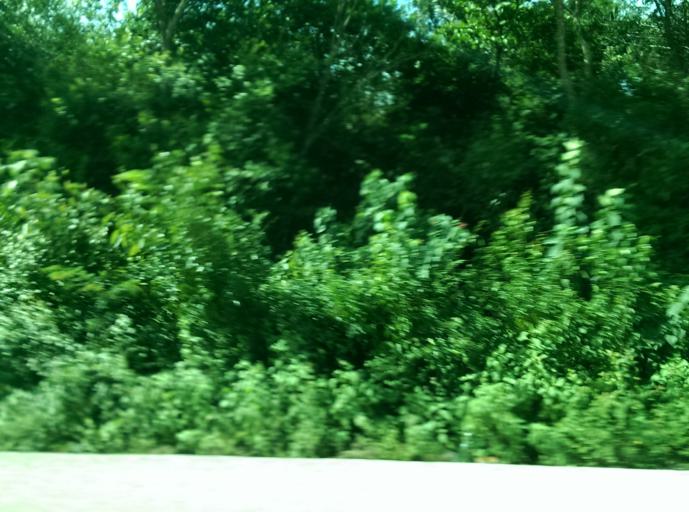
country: MX
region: Quintana Roo
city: Tulum
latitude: 20.2223
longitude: -87.4563
